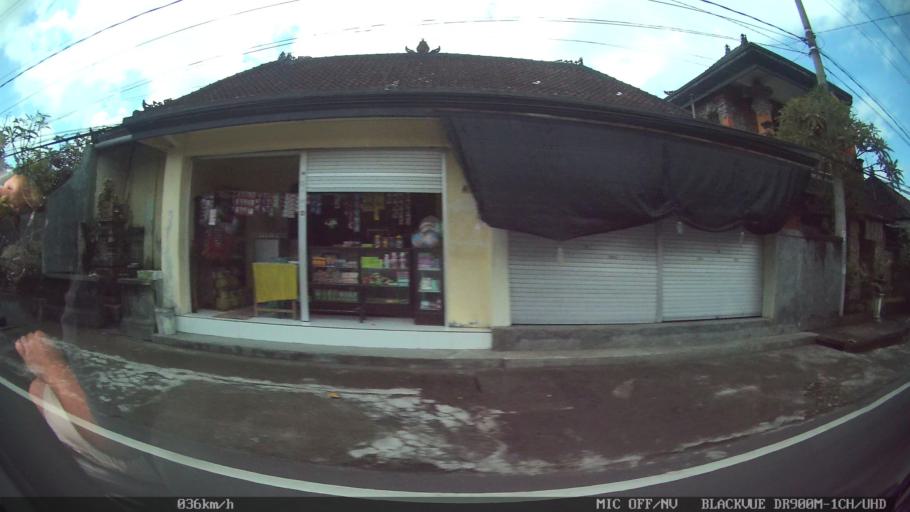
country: ID
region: Bali
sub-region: Kabupaten Gianyar
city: Ubud
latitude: -8.5548
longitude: 115.2871
